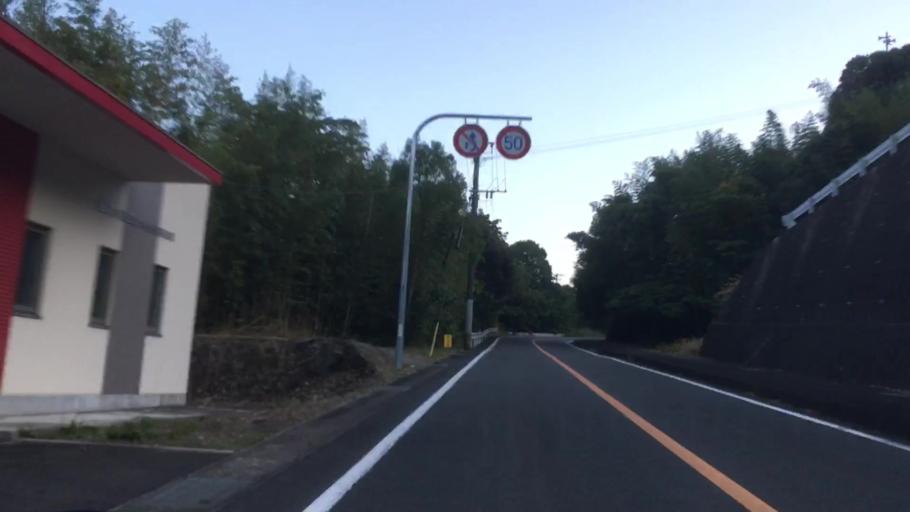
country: JP
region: Nagasaki
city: Sasebo
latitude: 32.9940
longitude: 129.7243
